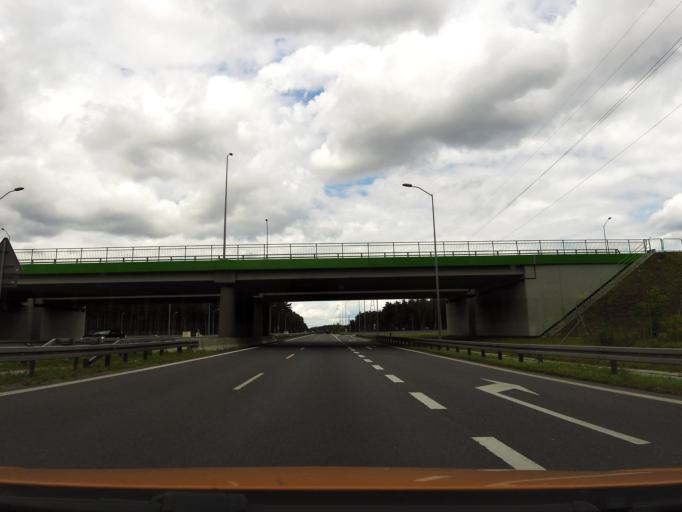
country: PL
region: West Pomeranian Voivodeship
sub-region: Powiat gryfinski
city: Stare Czarnowo
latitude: 53.3943
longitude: 14.7181
